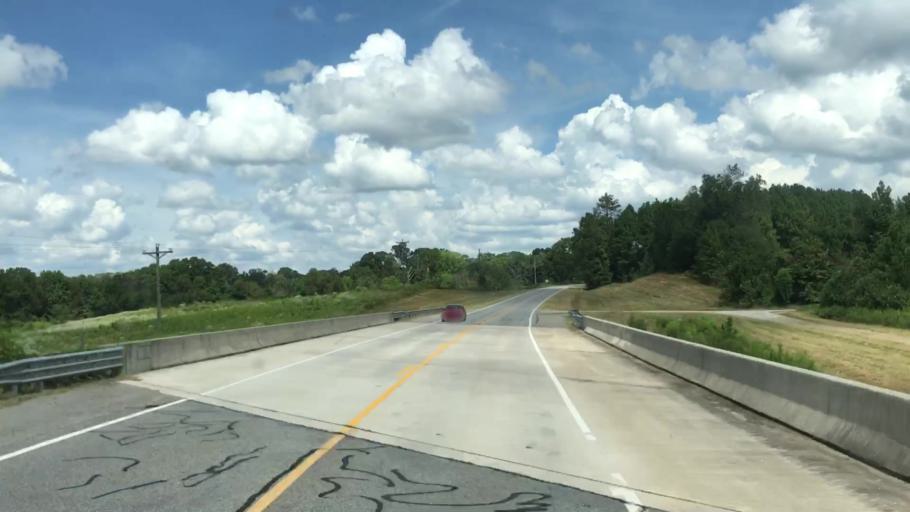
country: US
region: Georgia
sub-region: Oconee County
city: Watkinsville
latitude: 33.7363
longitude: -83.3034
